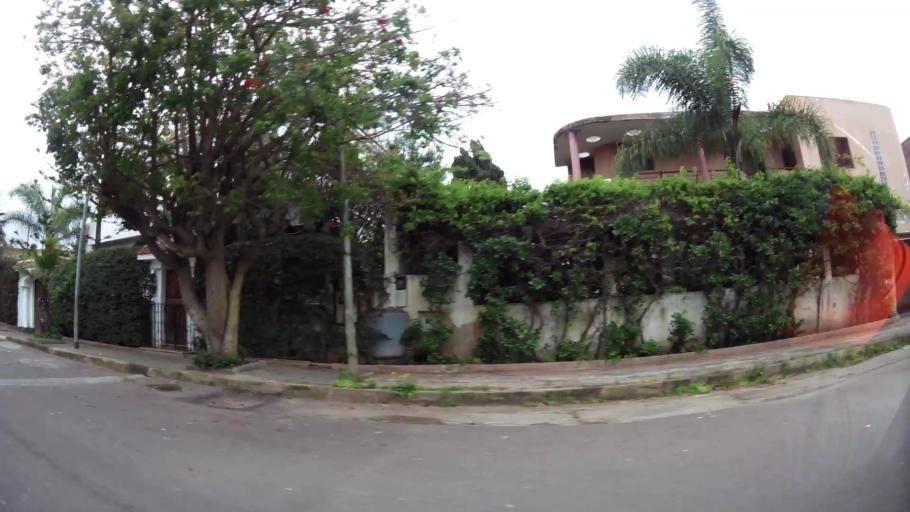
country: MA
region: Grand Casablanca
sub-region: Casablanca
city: Casablanca
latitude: 33.5469
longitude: -7.6394
